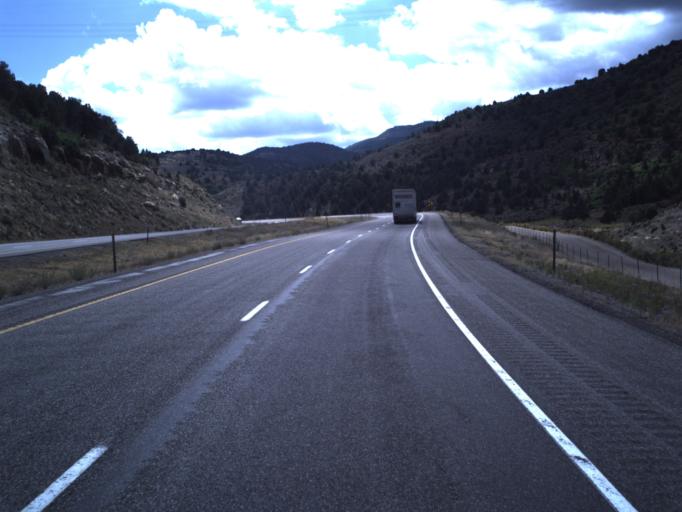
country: US
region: Utah
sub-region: Sevier County
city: Salina
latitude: 38.8157
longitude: -111.5367
